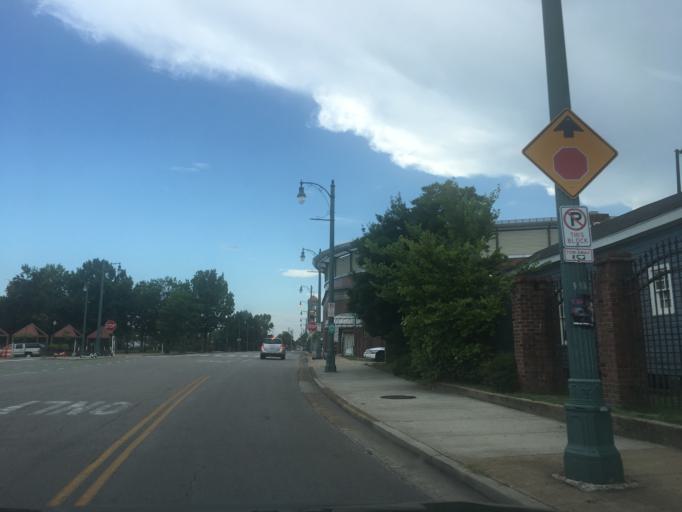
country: US
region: Tennessee
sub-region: Shelby County
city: Memphis
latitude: 35.1400
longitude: -90.0494
